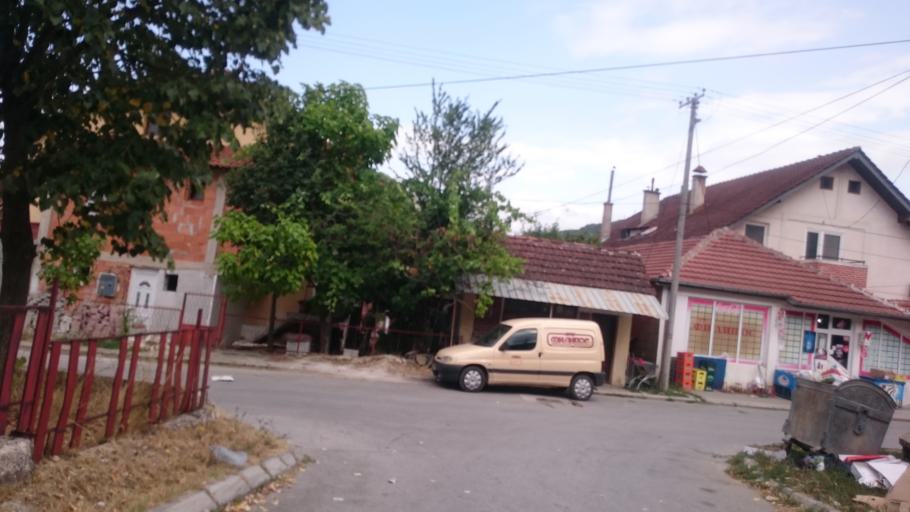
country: MK
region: Makedonski Brod
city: Makedonski Brod
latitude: 41.5141
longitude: 21.2162
